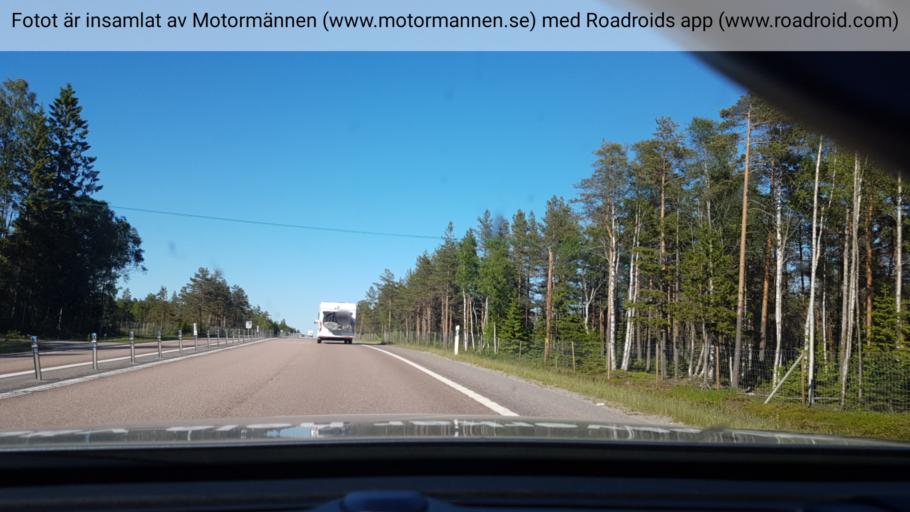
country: SE
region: Vaesternorrland
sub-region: Haernoesands Kommun
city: Haernoesand
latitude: 62.5652
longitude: 17.7320
